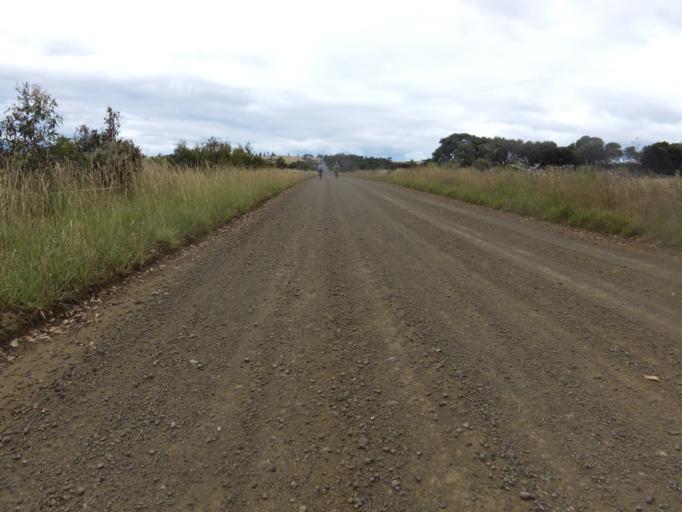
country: AU
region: Victoria
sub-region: Bass Coast
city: Cowes
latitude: -38.3853
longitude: 145.3132
